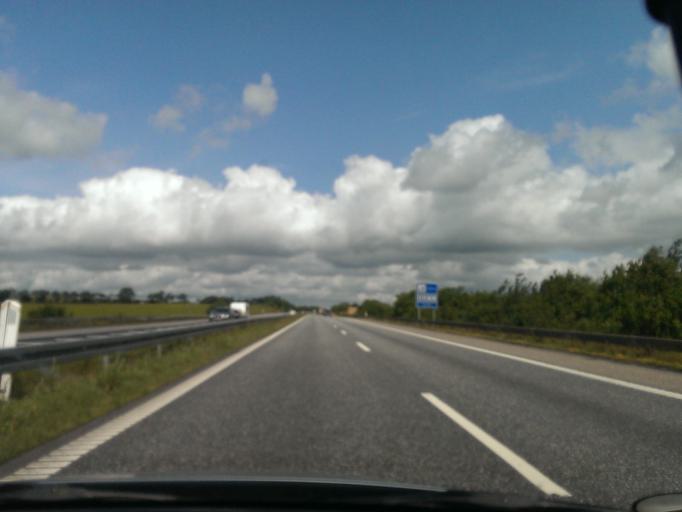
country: DK
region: North Denmark
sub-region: Mariagerfjord Kommune
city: Hobro
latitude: 56.7220
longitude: 9.7182
